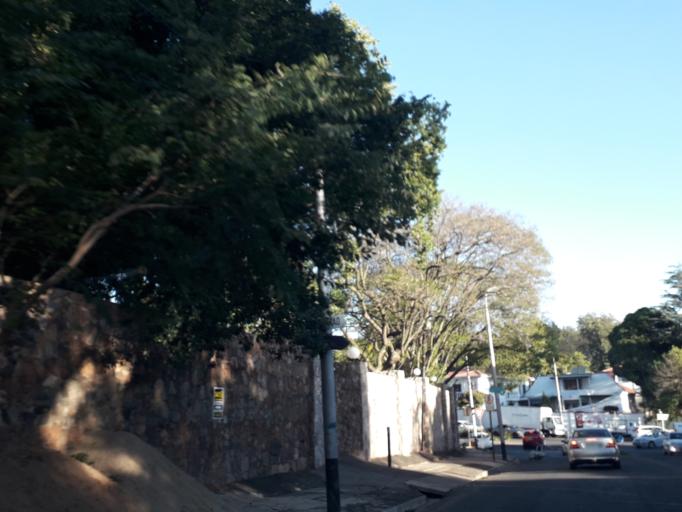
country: ZA
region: Gauteng
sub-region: City of Johannesburg Metropolitan Municipality
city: Johannesburg
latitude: -26.1783
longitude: 28.0211
